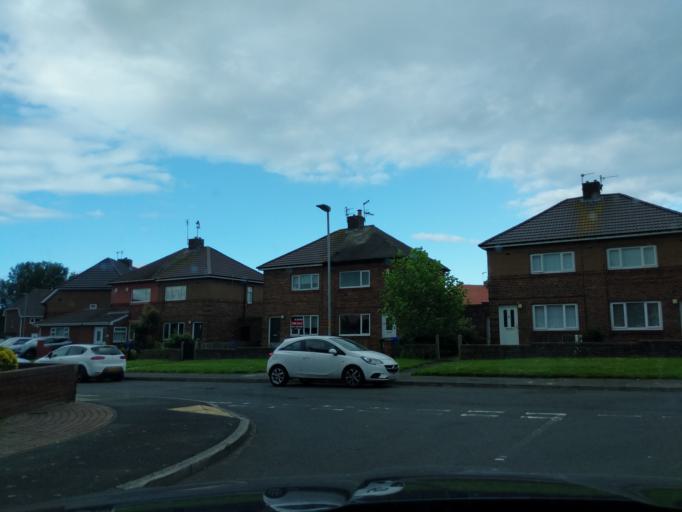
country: GB
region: England
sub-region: Northumberland
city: Seaton Delaval
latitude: 55.0854
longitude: -1.5185
